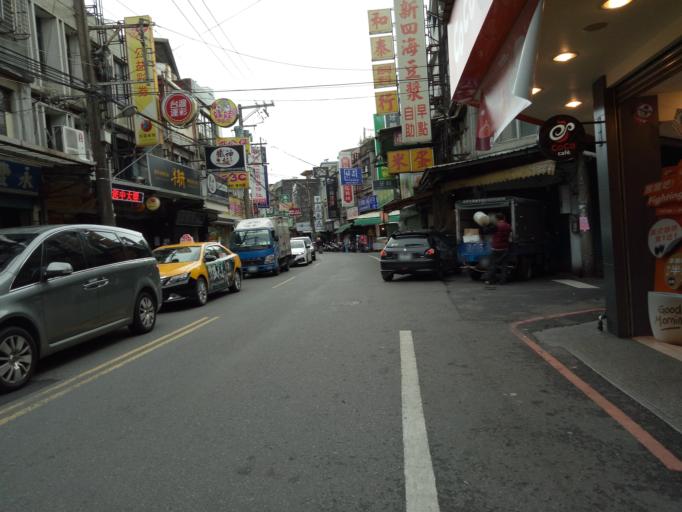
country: TW
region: Taiwan
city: Taoyuan City
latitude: 24.9593
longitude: 121.2965
